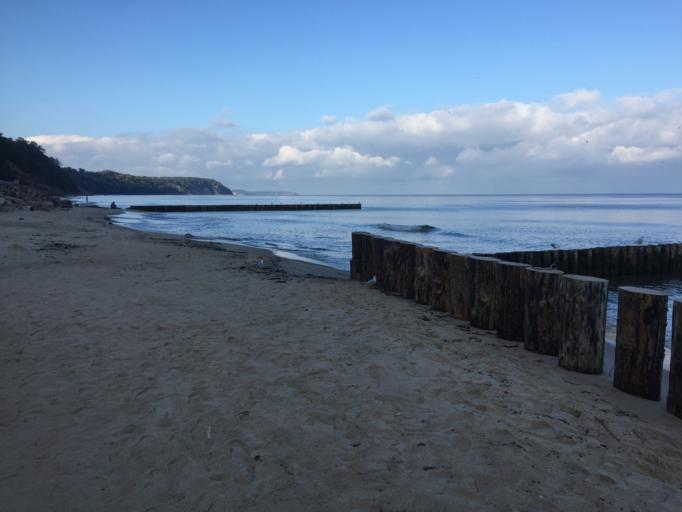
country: RU
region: Kaliningrad
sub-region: Gorod Svetlogorsk
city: Svetlogorsk
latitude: 54.9461
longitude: 20.1475
